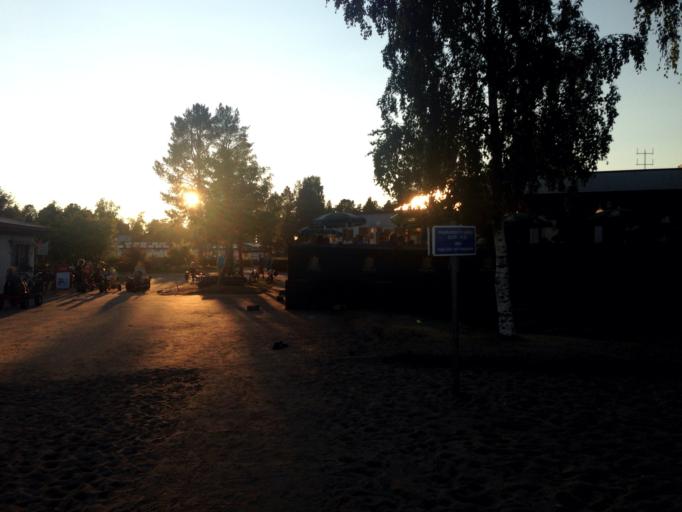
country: SE
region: Vaesterbotten
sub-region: Skelleftea Kommun
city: Byske
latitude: 64.9471
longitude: 21.2383
